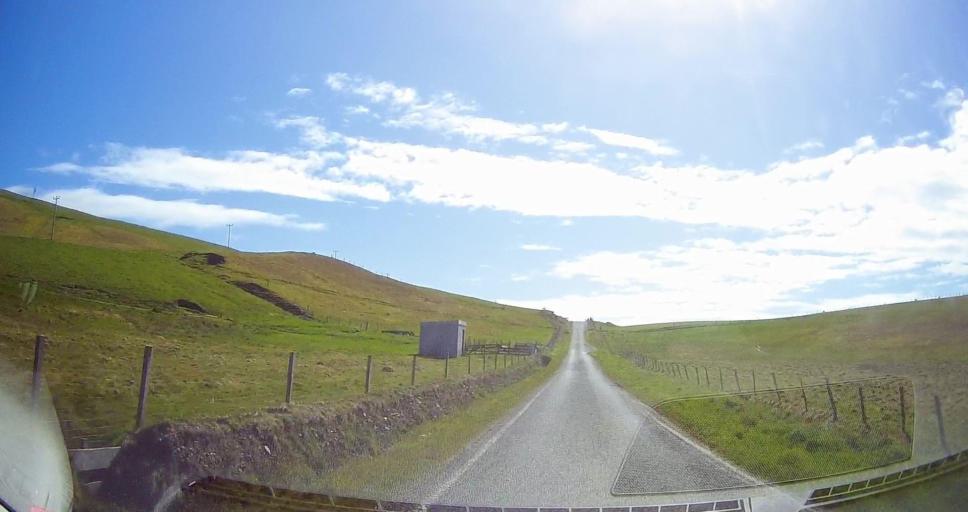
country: GB
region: Scotland
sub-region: Shetland Islands
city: Sandwick
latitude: 59.9632
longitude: -1.3219
